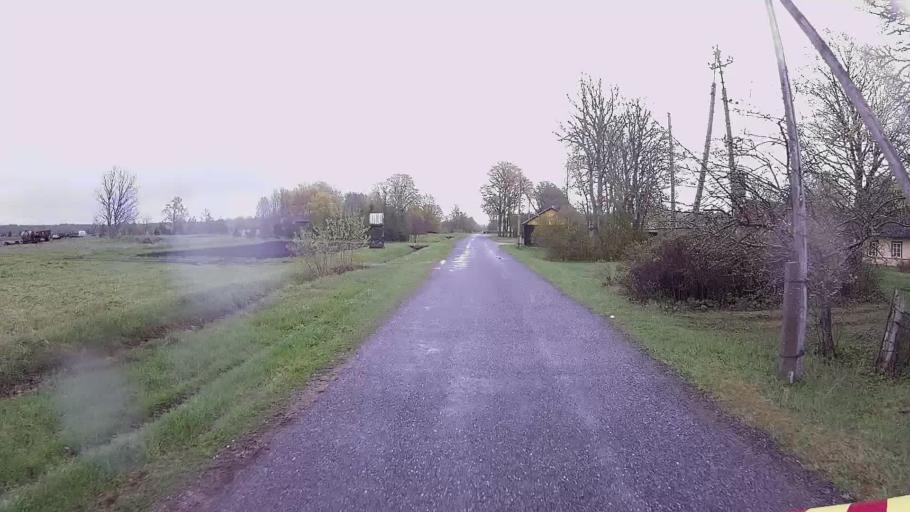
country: EE
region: Hiiumaa
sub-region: Kaerdla linn
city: Kardla
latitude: 58.6974
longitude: 22.5406
